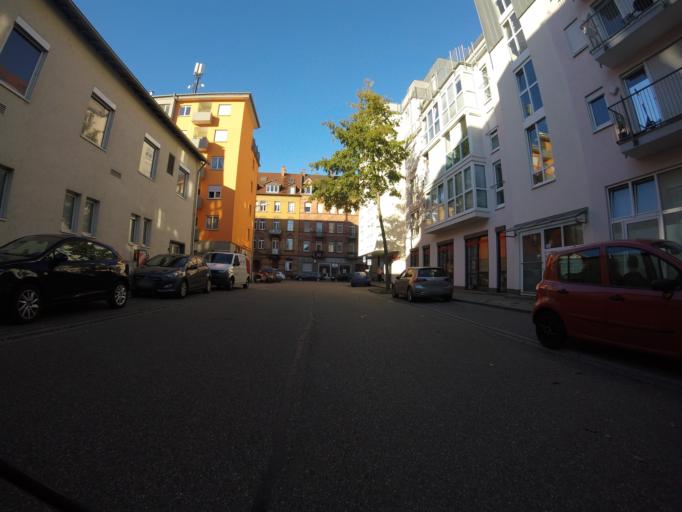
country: DE
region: Baden-Wuerttemberg
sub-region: Karlsruhe Region
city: Karlsruhe
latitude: 49.0101
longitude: 8.4241
